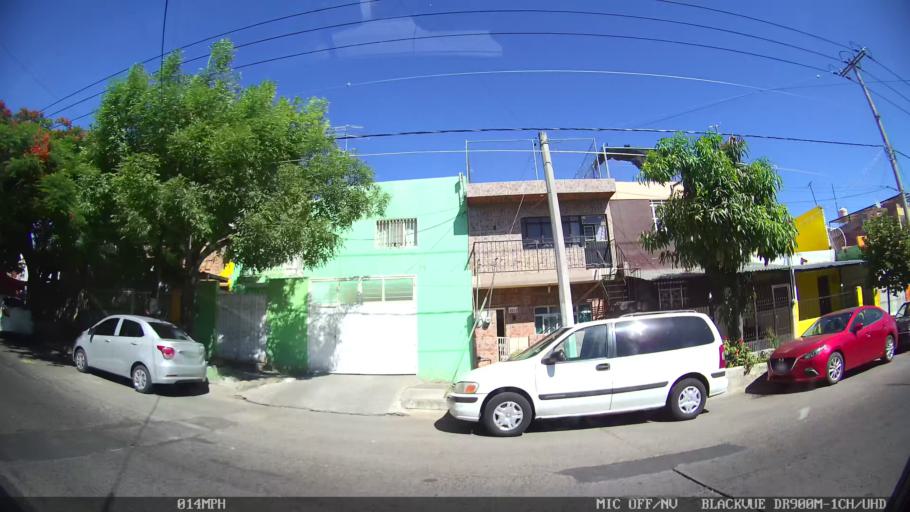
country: MX
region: Jalisco
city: Tlaquepaque
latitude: 20.6979
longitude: -103.2872
